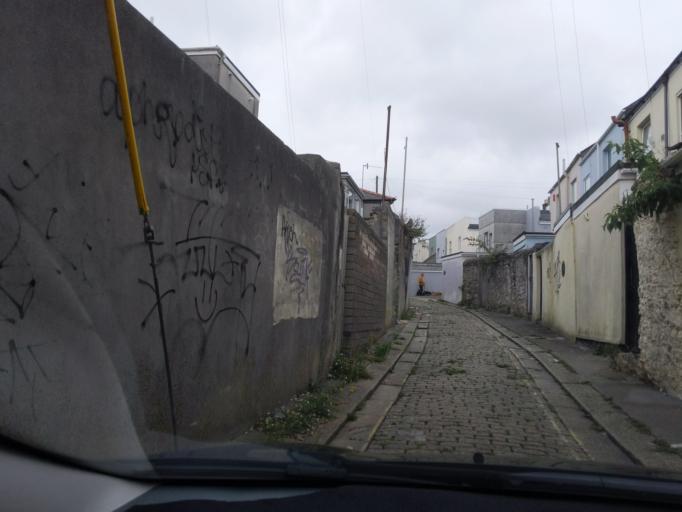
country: GB
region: England
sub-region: Plymouth
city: Plymouth
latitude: 50.3754
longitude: -4.1329
